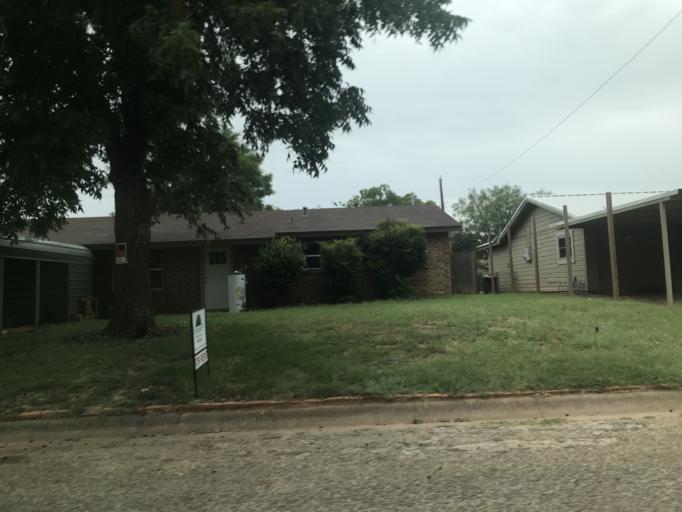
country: US
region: Texas
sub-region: Taylor County
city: Abilene
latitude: 32.4142
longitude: -99.7839
